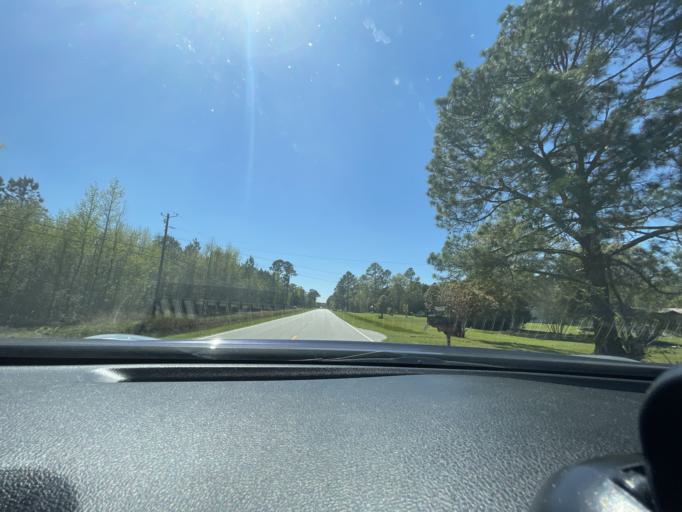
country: US
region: Georgia
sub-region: Chatham County
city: Bloomingdale
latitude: 32.0972
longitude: -81.2930
